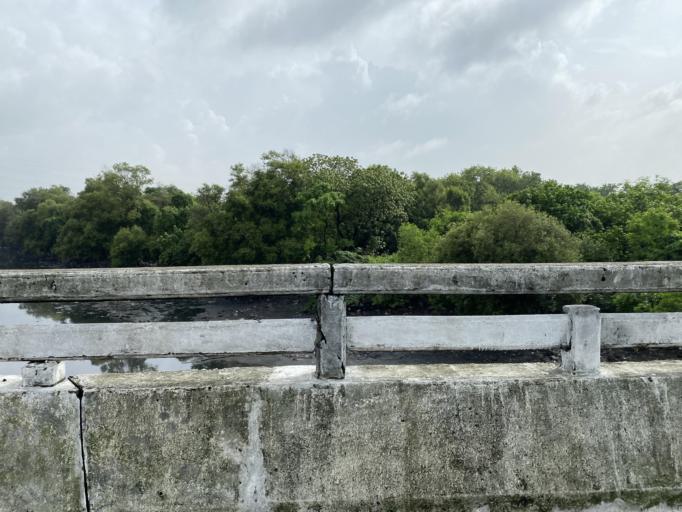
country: IN
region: Maharashtra
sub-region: Mumbai Suburban
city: Borivli
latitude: 19.2619
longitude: 72.8544
